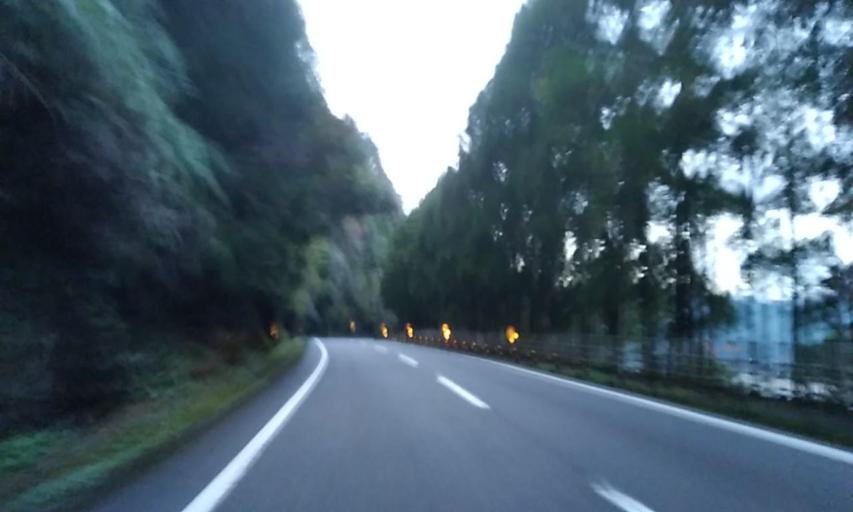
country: JP
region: Wakayama
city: Shingu
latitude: 33.7308
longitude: 135.9468
